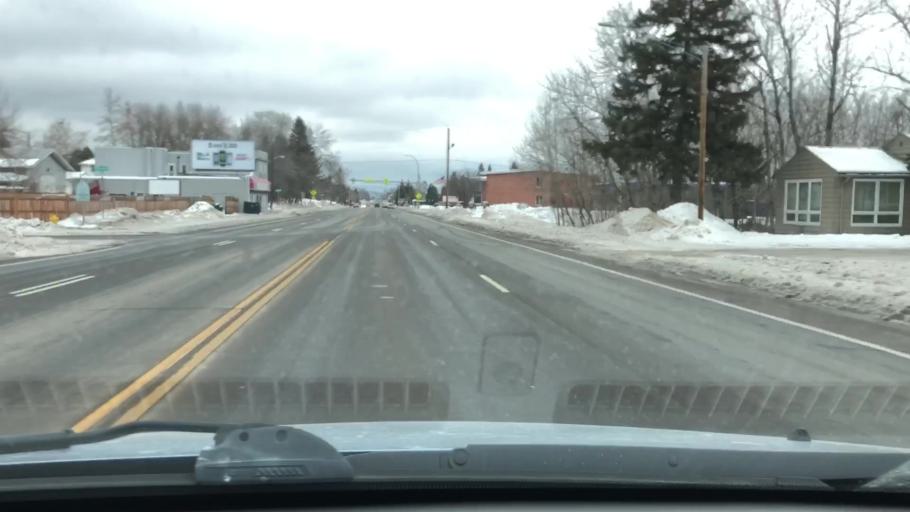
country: US
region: Minnesota
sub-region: Saint Louis County
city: Proctor
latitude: 46.7207
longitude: -92.1951
